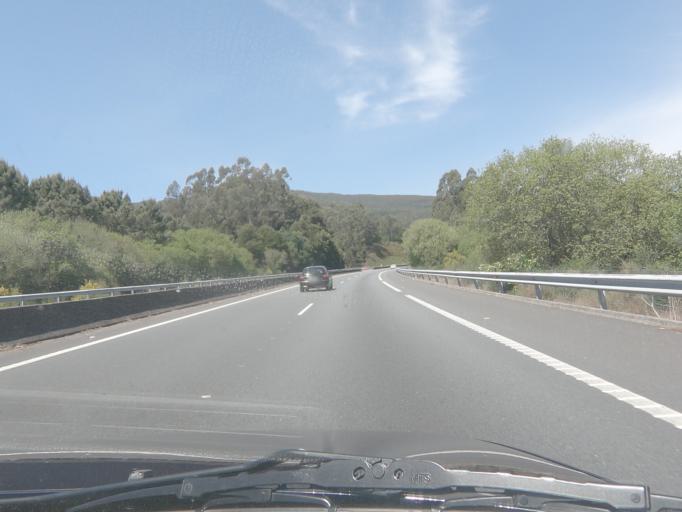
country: ES
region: Galicia
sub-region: Provincia de Pontevedra
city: Pontevedra
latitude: 42.4692
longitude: -8.6564
